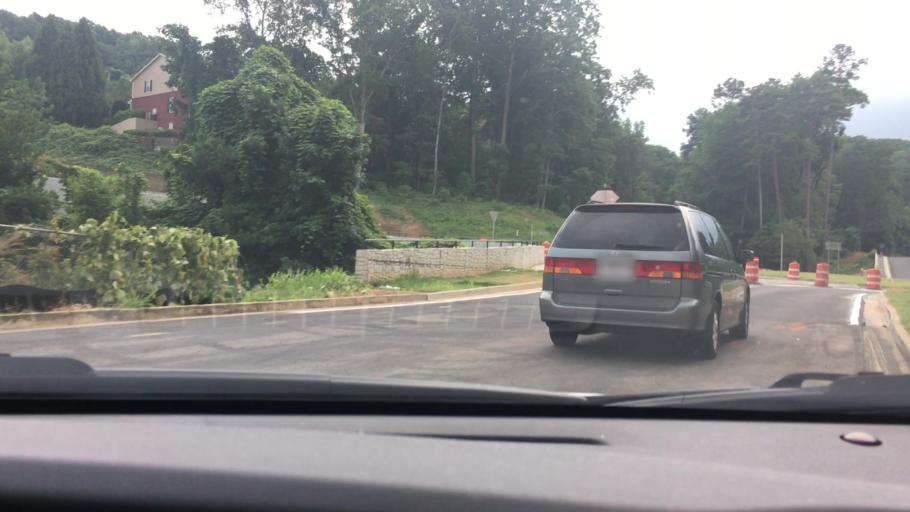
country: US
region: Georgia
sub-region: Cobb County
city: Kennesaw
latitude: 34.0039
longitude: -84.5728
